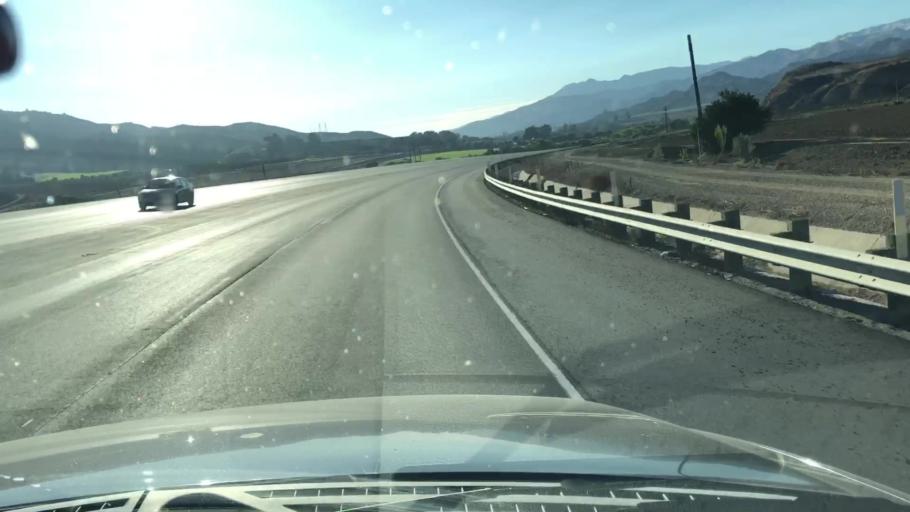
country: US
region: California
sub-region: Los Angeles County
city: Val Verde
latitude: 34.4027
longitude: -118.7077
